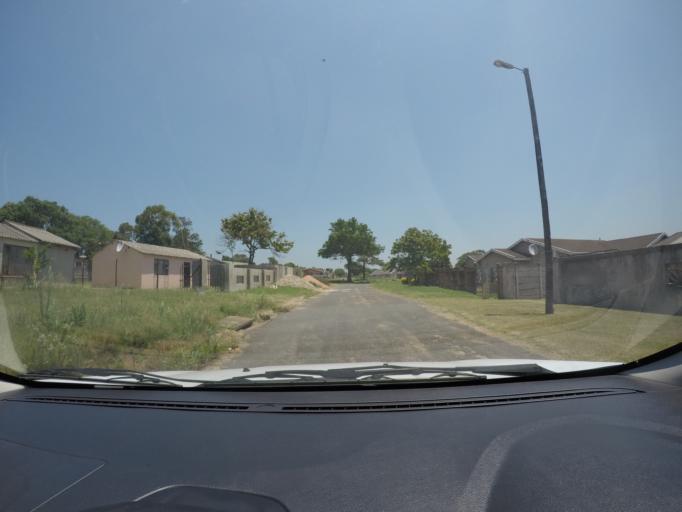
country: ZA
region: KwaZulu-Natal
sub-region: uThungulu District Municipality
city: eSikhawini
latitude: -28.8805
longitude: 31.8928
